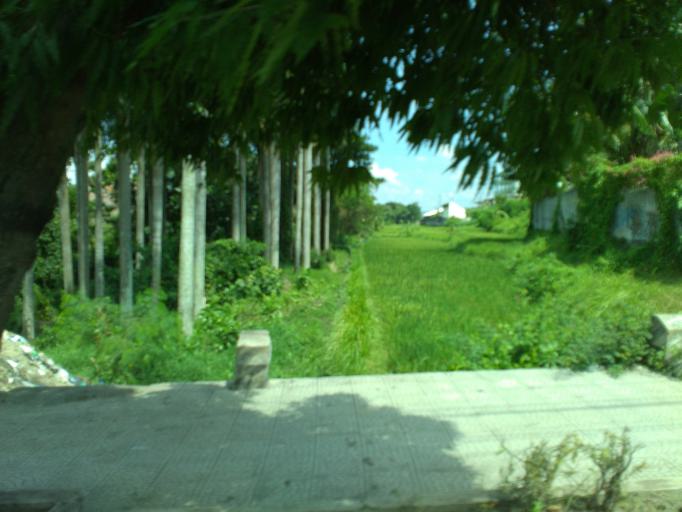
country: ID
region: Central Java
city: Klaten
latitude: -7.7157
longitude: 110.5873
